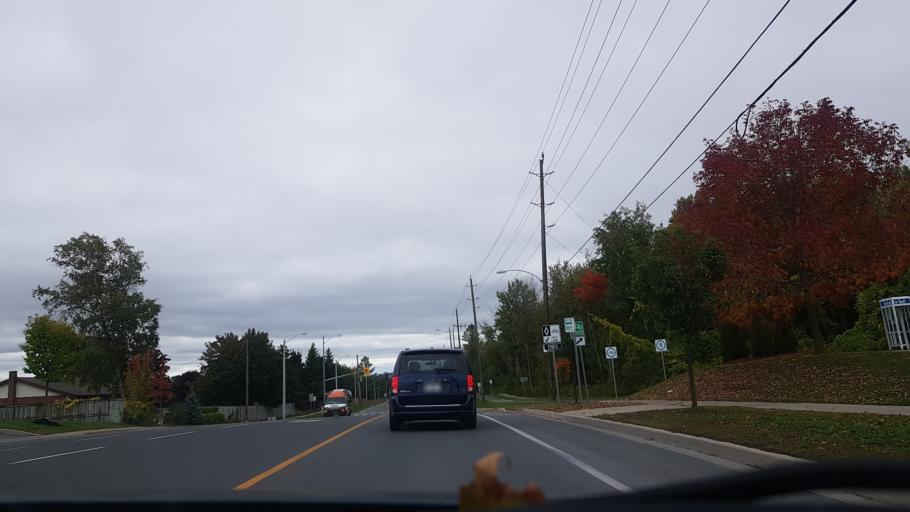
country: CA
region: Ontario
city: Peterborough
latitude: 44.2752
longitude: -78.3719
